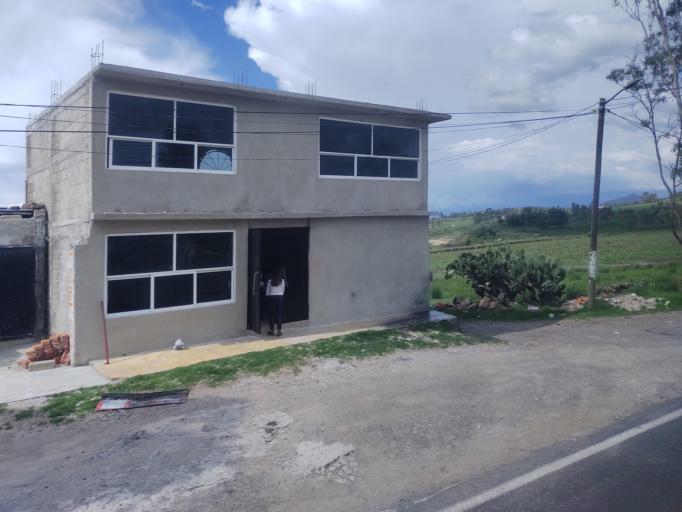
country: MX
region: Mexico
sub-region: Aculco
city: El Colorado
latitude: 20.0921
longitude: -99.7822
